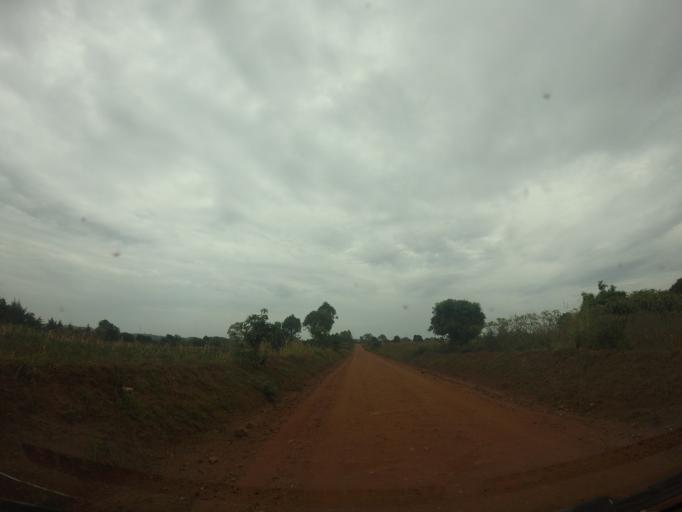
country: UG
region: Northern Region
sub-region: Arua District
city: Arua
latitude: 2.8052
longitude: 30.8798
